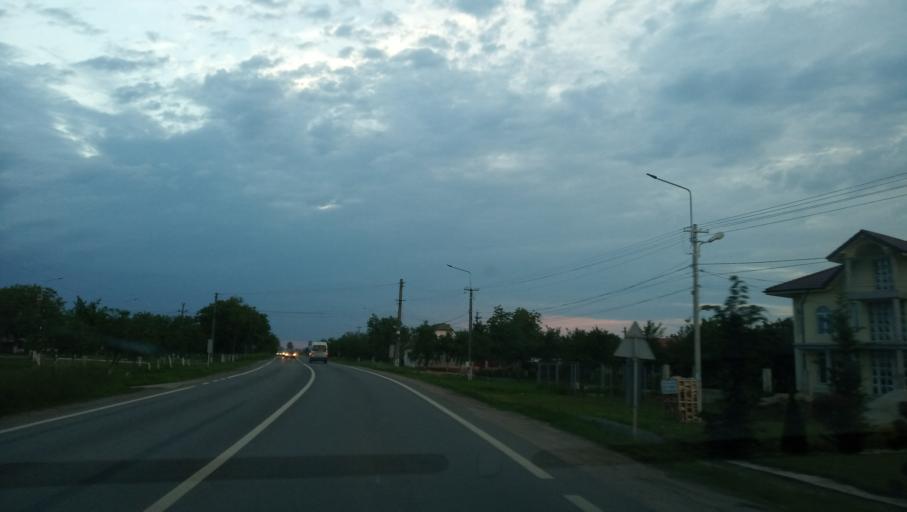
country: RO
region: Timis
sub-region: Comuna Jebel
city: Jebel
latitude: 45.5679
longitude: 21.2087
